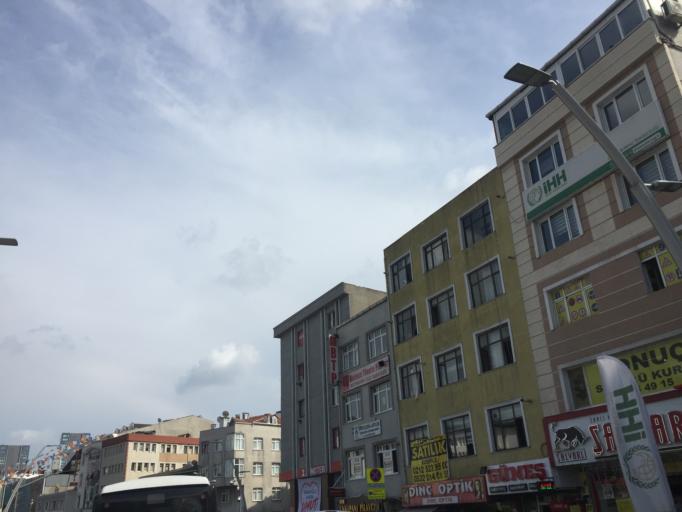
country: TR
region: Istanbul
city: Zeytinburnu
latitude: 40.9953
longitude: 28.9026
